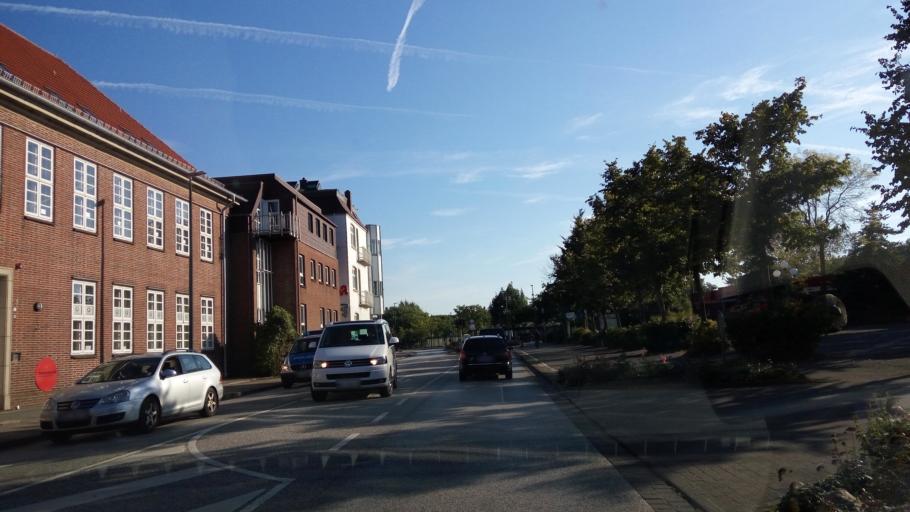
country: DE
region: Schleswig-Holstein
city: Eckernforde
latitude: 54.4687
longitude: 9.8357
